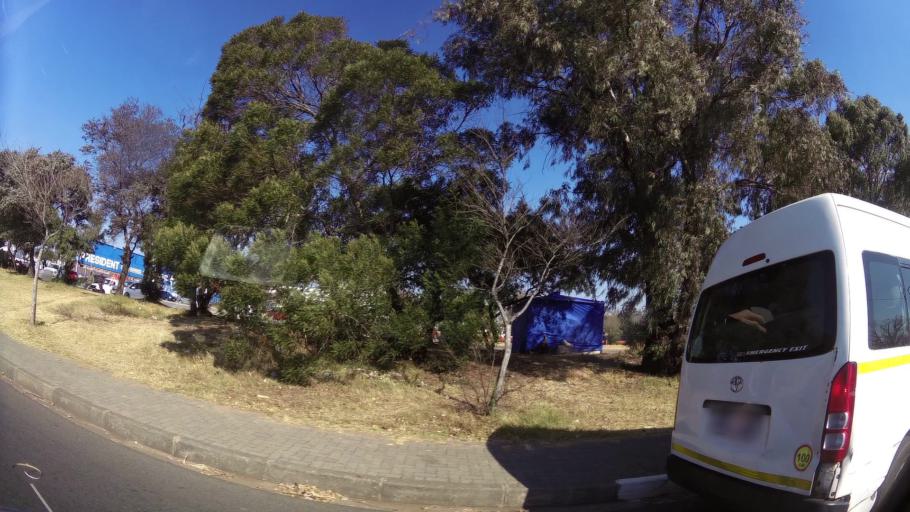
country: ZA
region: Gauteng
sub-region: City of Johannesburg Metropolitan Municipality
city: Johannesburg
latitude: -26.2573
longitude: 27.9963
